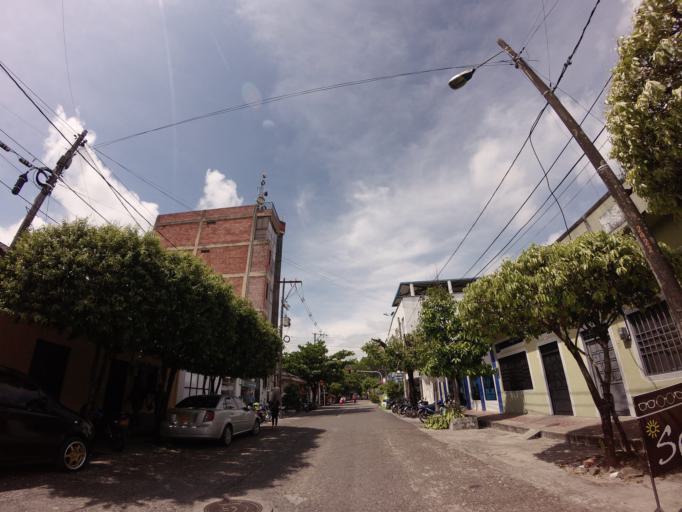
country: CO
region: Caldas
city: La Dorada
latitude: 5.4512
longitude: -74.6627
